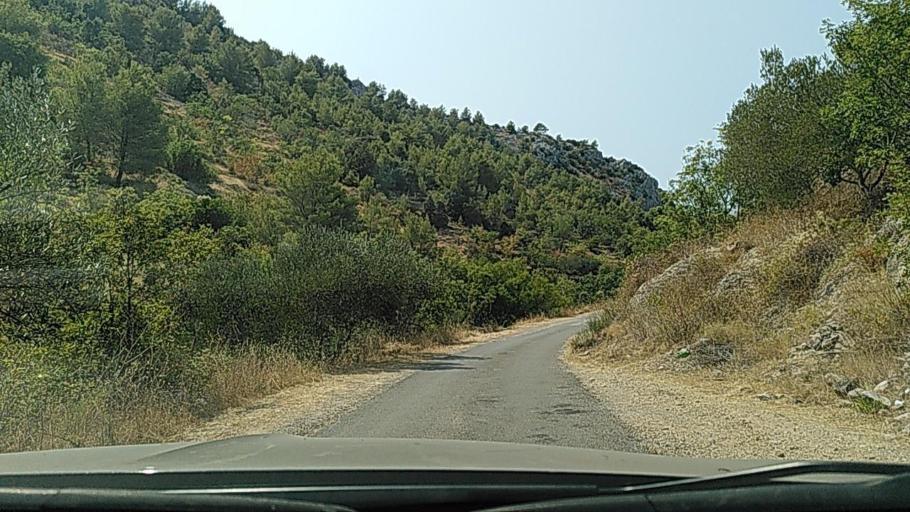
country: HR
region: Splitsko-Dalmatinska
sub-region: Grad Hvar
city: Hvar
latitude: 43.1664
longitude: 16.5094
